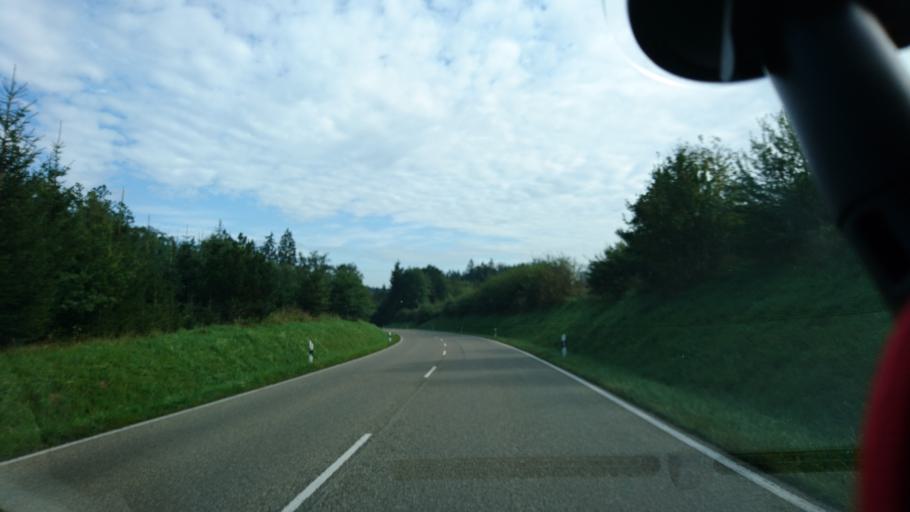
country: DE
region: Baden-Wuerttemberg
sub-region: Regierungsbezirk Stuttgart
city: Grosserlach
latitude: 49.0590
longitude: 9.5236
